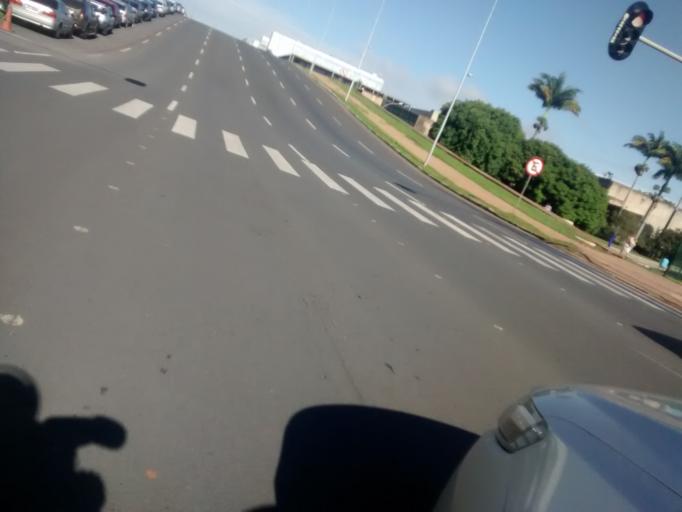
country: BR
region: Federal District
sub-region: Brasilia
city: Brasilia
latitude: -15.7992
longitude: -47.8624
